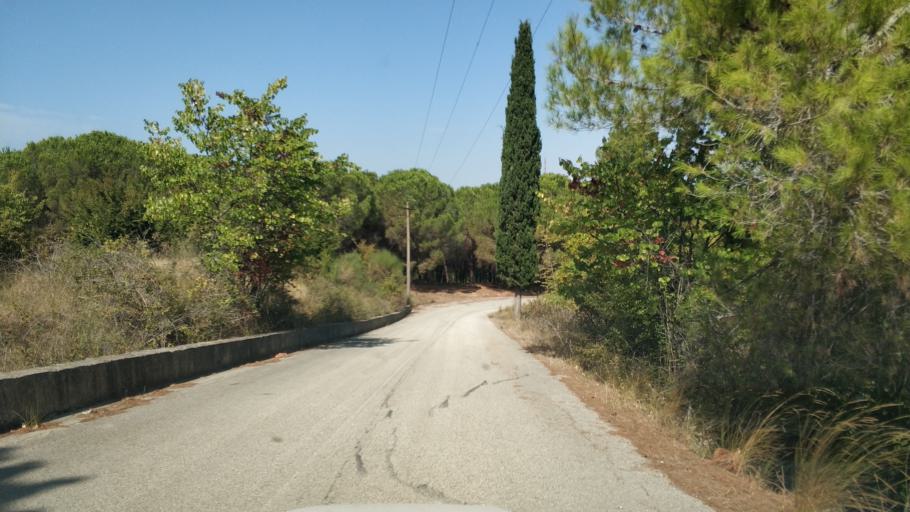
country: AL
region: Fier
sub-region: Rrethi i Lushnjes
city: Kolonje
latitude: 40.8192
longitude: 19.5939
